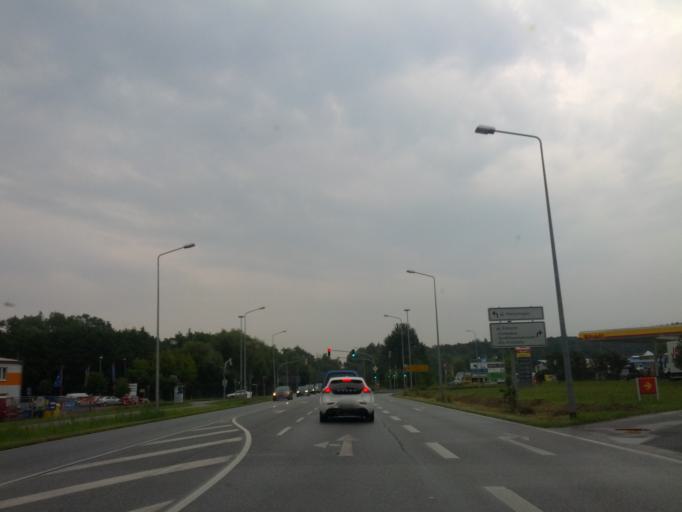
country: DE
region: Mecklenburg-Vorpommern
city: Bad Doberan
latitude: 54.1069
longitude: 11.9272
